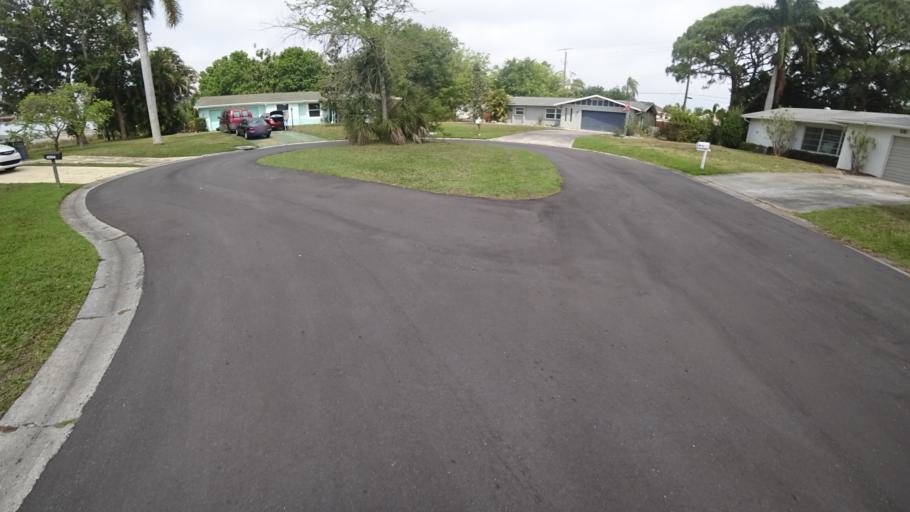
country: US
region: Florida
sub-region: Manatee County
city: West Bradenton
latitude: 27.4937
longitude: -82.6234
